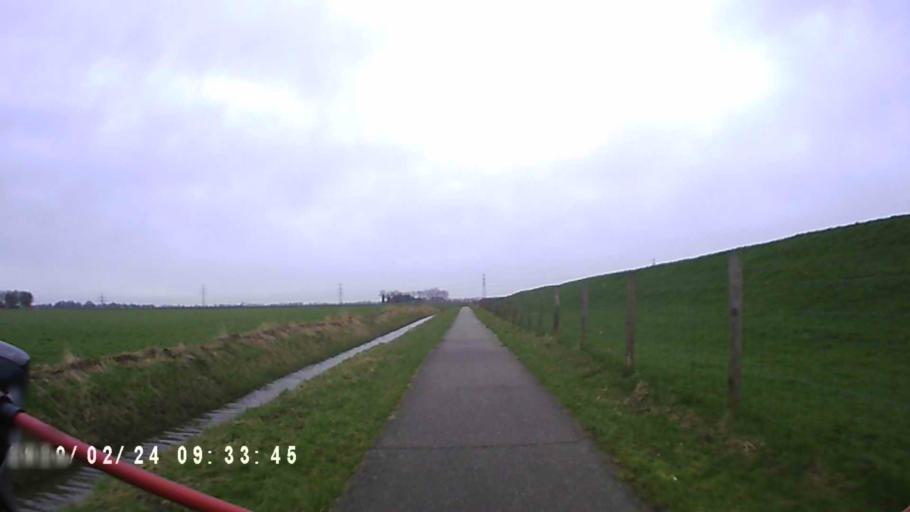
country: NL
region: Groningen
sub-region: Gemeente Winsum
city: Winsum
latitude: 53.3007
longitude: 6.5005
